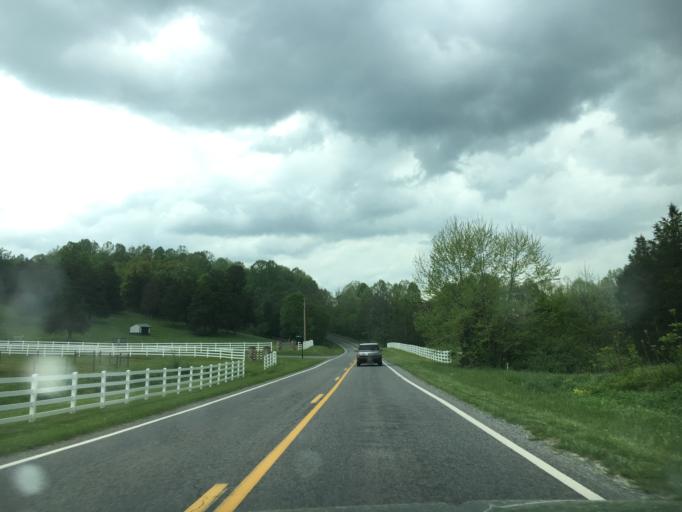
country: US
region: Virginia
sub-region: Campbell County
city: Rustburg
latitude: 37.3242
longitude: -79.1262
